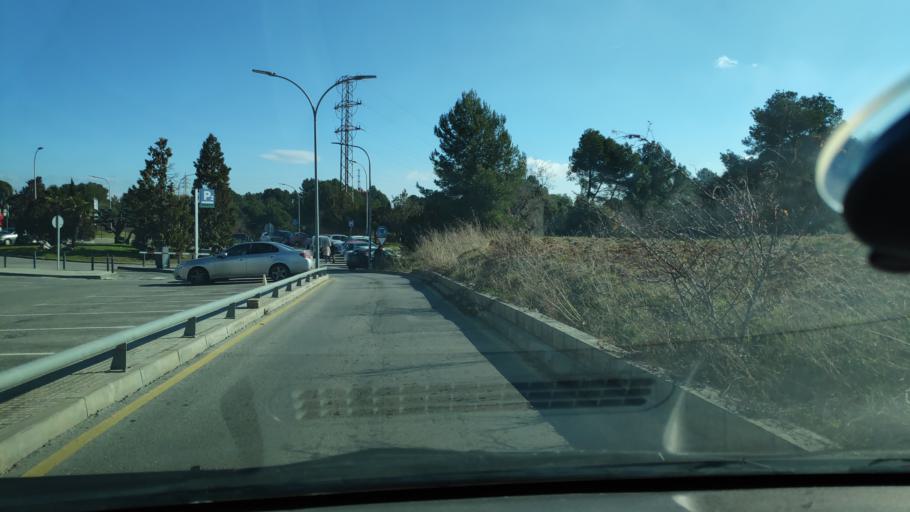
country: ES
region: Catalonia
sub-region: Provincia de Barcelona
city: Sant Quirze del Valles
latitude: 41.5558
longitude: 2.0532
